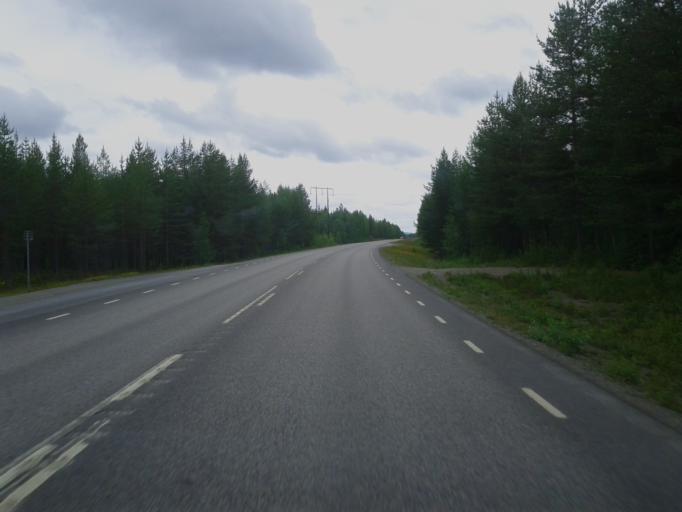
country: SE
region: Vaesterbotten
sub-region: Skelleftea Kommun
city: Langsele
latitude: 64.9260
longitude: 20.0165
